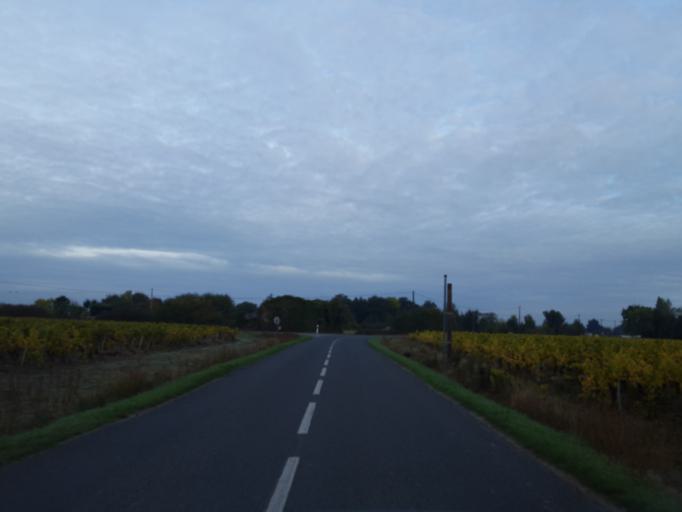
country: FR
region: Pays de la Loire
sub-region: Departement de la Loire-Atlantique
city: Saint-Julien-de-Concelles
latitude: 47.2392
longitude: -1.3909
